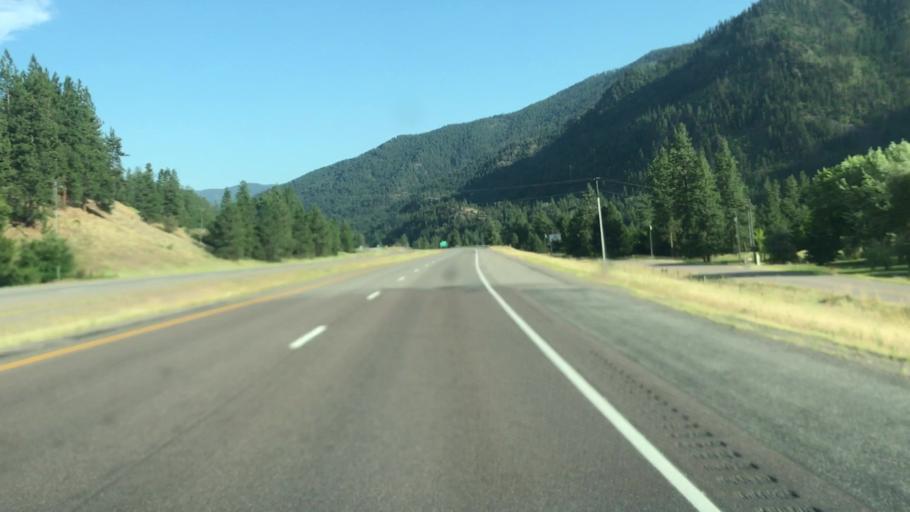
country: US
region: Montana
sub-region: Missoula County
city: Frenchtown
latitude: 47.0126
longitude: -114.5026
